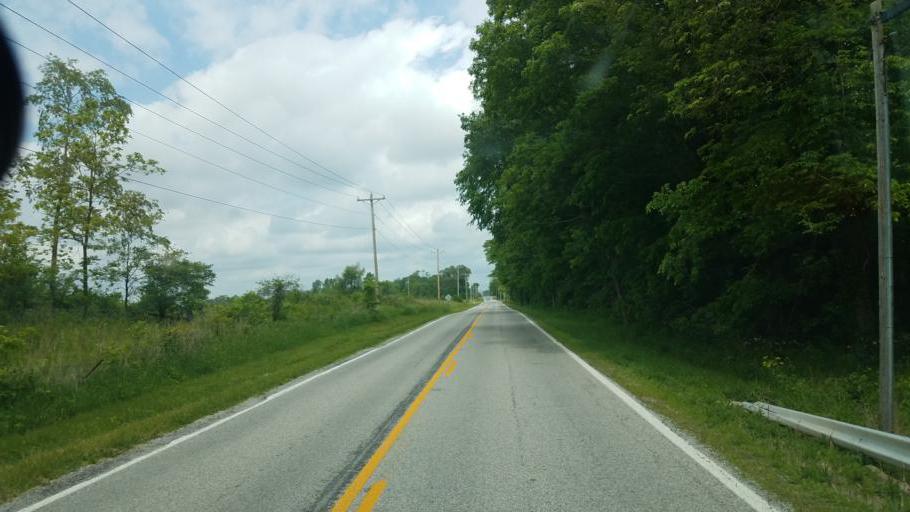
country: US
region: Ohio
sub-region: Marion County
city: Prospect
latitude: 40.4145
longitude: -83.1988
